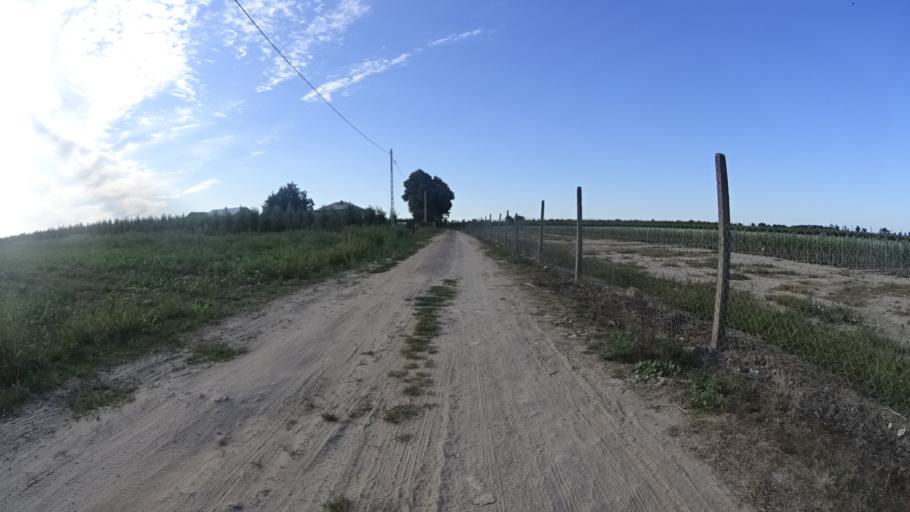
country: PL
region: Masovian Voivodeship
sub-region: Powiat bialobrzeski
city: Wysmierzyce
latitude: 51.6807
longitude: 20.8158
